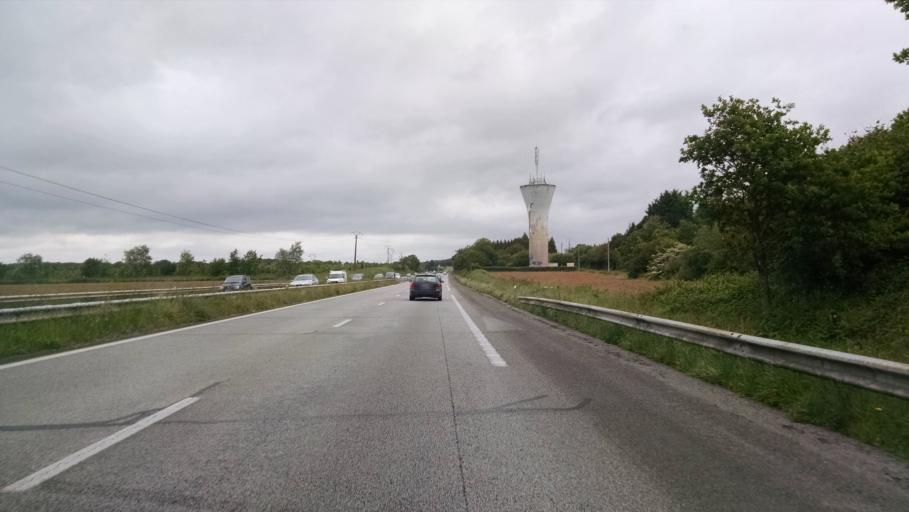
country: FR
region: Brittany
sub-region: Departement du Finistere
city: Landrevarzec
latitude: 48.0883
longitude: -4.0395
